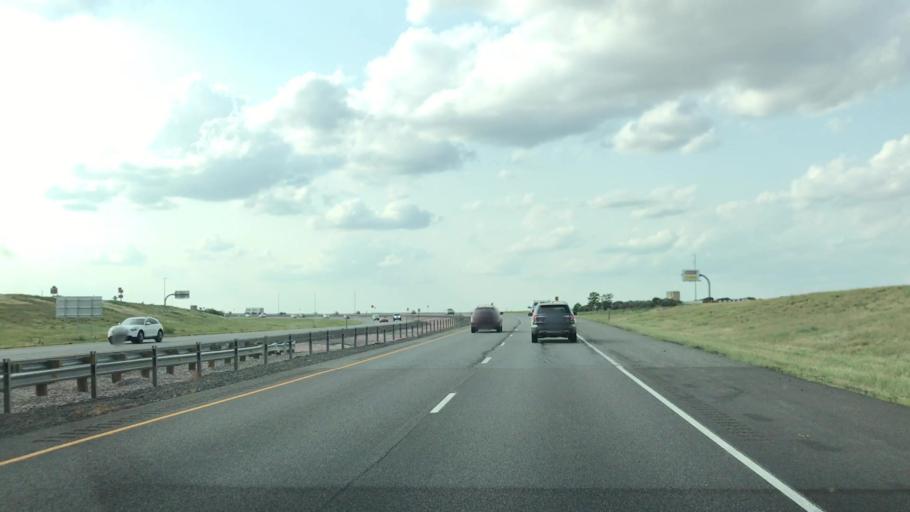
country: US
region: Colorado
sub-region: Adams County
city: Aurora
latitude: 39.8128
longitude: -104.7207
